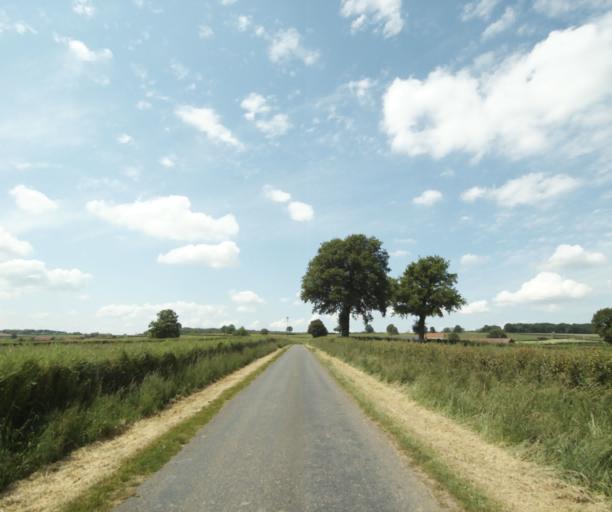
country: FR
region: Bourgogne
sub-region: Departement de Saone-et-Loire
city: Perrecy-les-Forges
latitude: 46.5835
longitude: 4.1440
